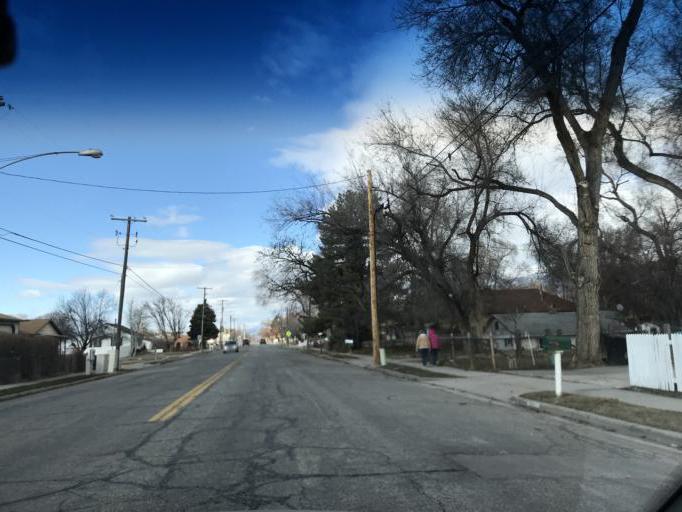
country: US
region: Utah
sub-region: Davis County
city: Woods Cross
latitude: 40.8722
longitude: -111.9021
